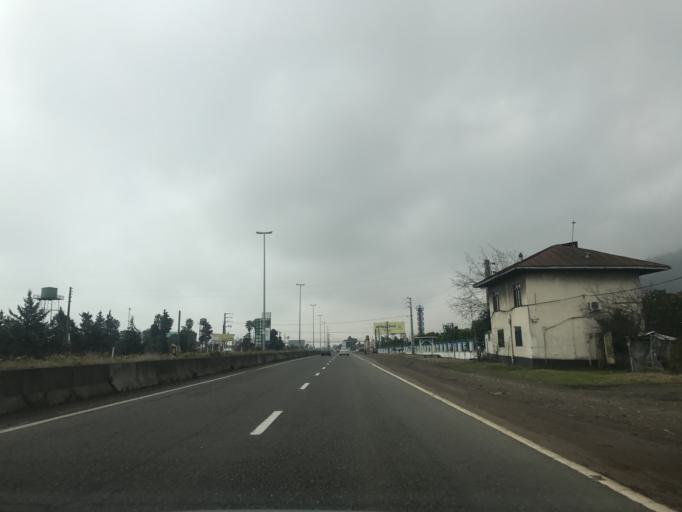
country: IR
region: Mazandaran
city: Ramsar
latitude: 36.9613
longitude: 50.5967
